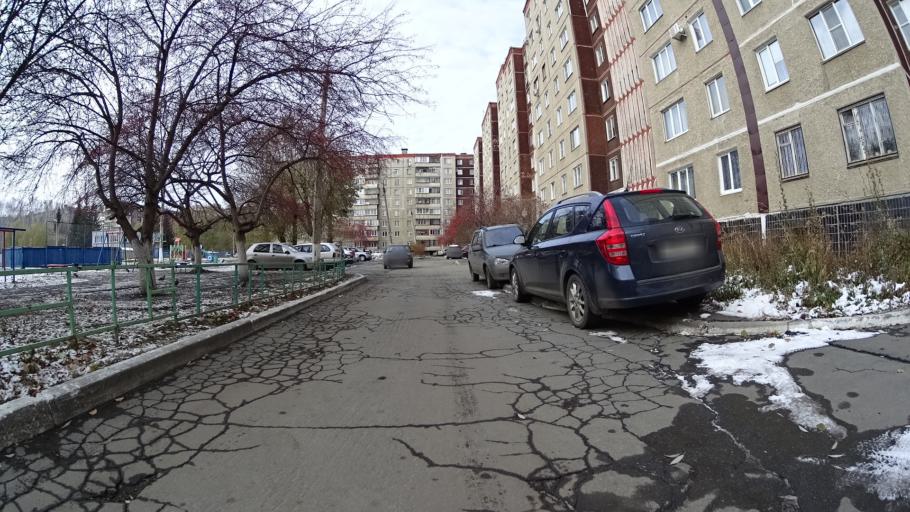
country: RU
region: Chelyabinsk
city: Roshchino
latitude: 55.1899
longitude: 61.2995
